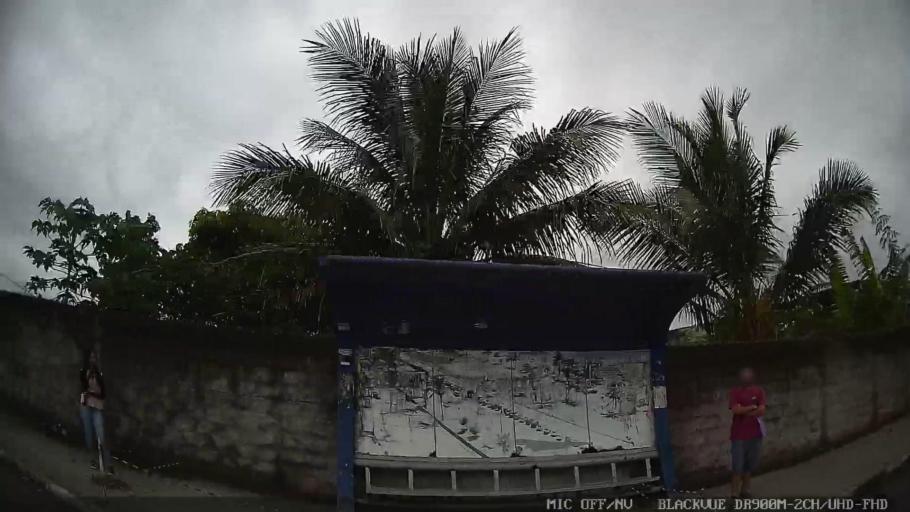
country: BR
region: Sao Paulo
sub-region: Sao Sebastiao
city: Sao Sebastiao
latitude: -23.7111
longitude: -45.4424
